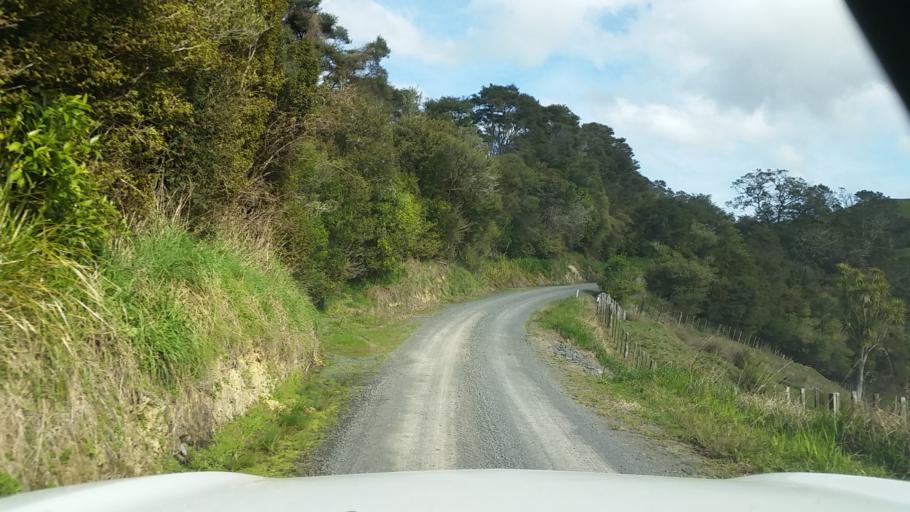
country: NZ
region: Waikato
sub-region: Hauraki District
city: Ngatea
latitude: -37.4789
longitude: 175.4545
